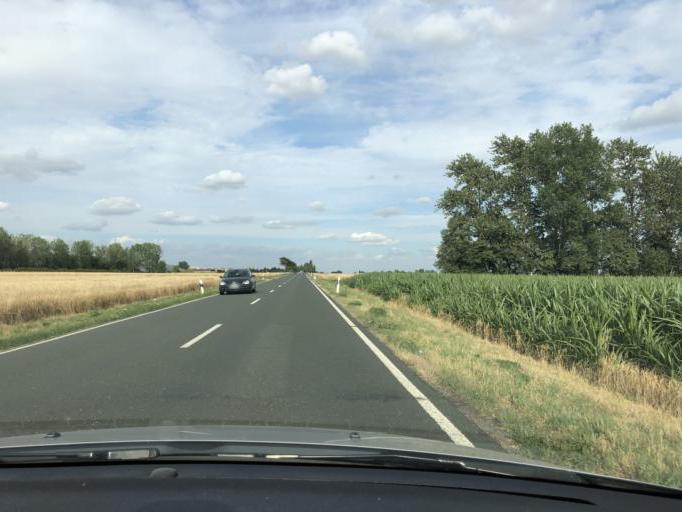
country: DE
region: Thuringia
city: Hainichen
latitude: 51.0349
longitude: 11.6208
